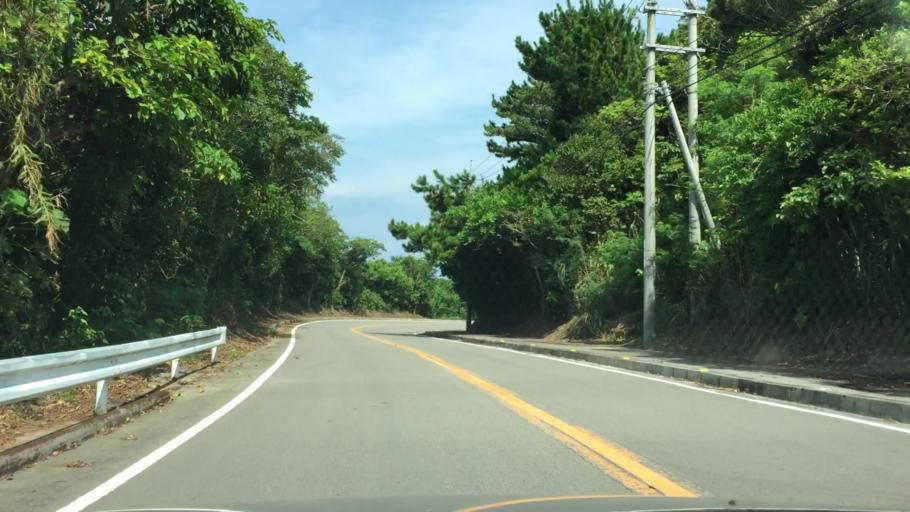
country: JP
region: Okinawa
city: Ishigaki
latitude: 24.5122
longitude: 124.2660
